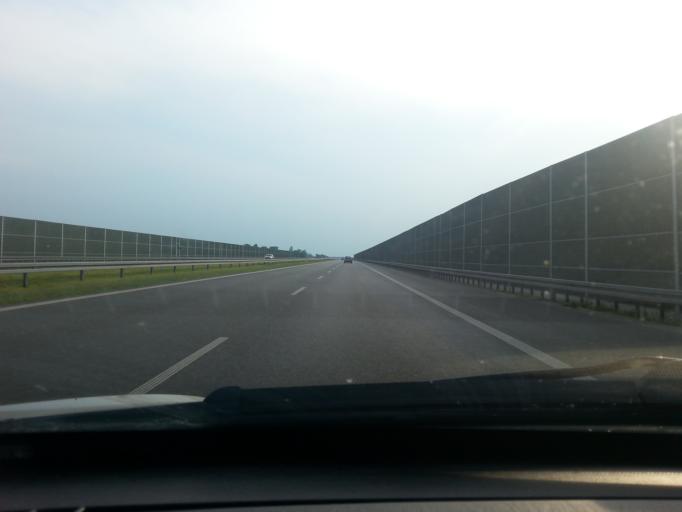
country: PL
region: Masovian Voivodeship
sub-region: Powiat warszawski zachodni
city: Bieniewice
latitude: 52.1416
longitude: 20.5915
